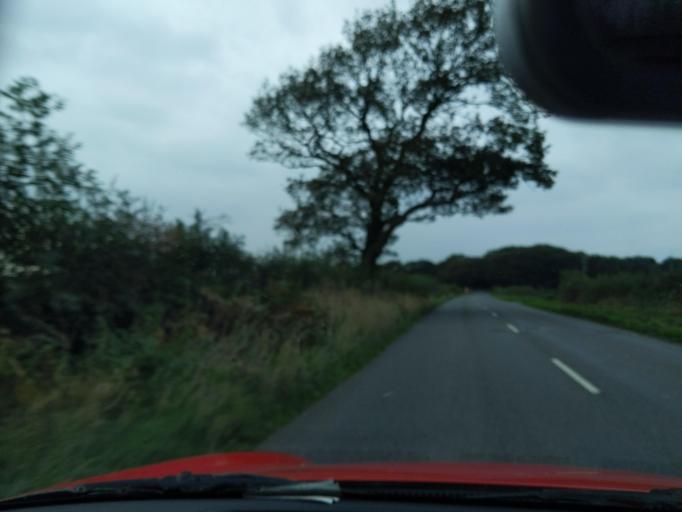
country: GB
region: England
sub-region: Devon
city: Okehampton
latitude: 50.7916
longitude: -4.0374
